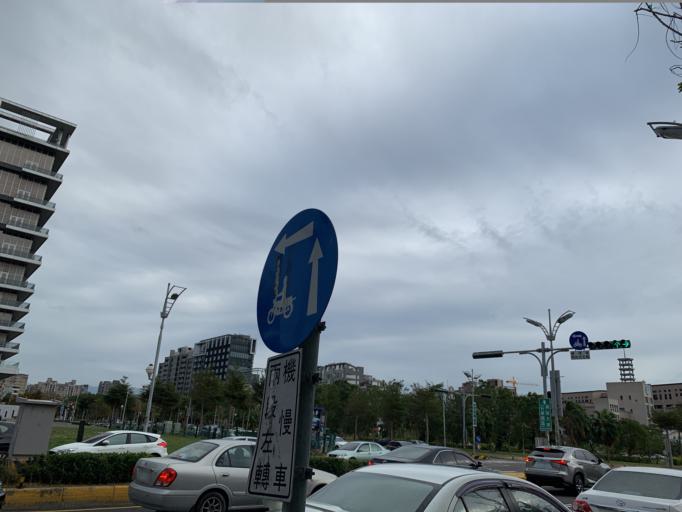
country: TW
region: Taiwan
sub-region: Hsinchu
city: Zhubei
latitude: 24.8156
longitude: 121.0196
